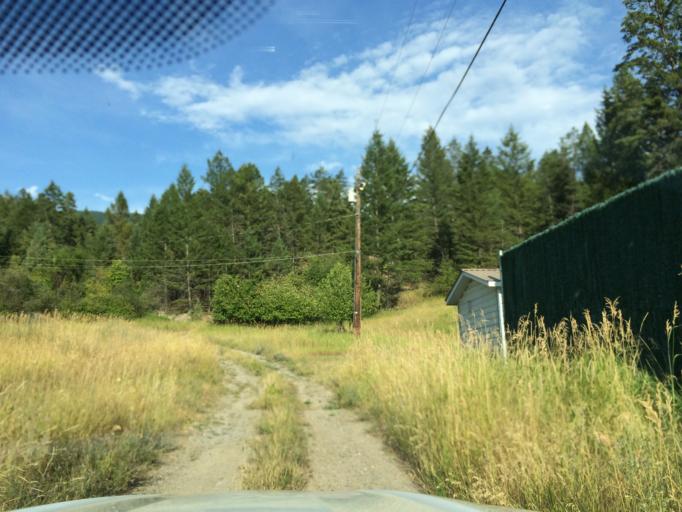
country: US
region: Montana
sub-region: Lincoln County
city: Eureka
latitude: 49.0006
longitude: -115.0548
